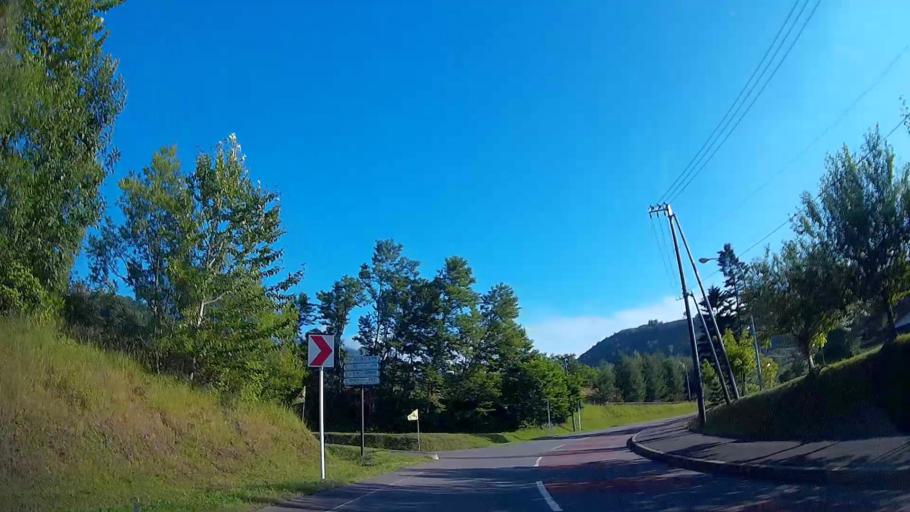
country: JP
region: Hokkaido
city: Date
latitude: 42.5642
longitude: 140.8133
